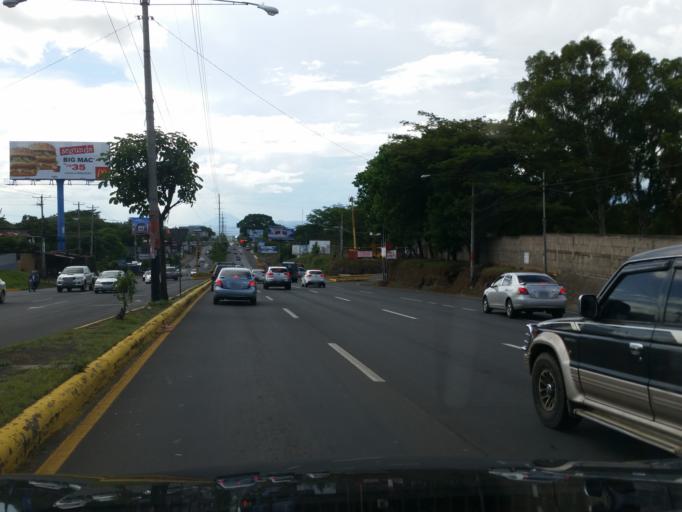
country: NI
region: Managua
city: Managua
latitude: 12.0906
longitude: -86.2346
